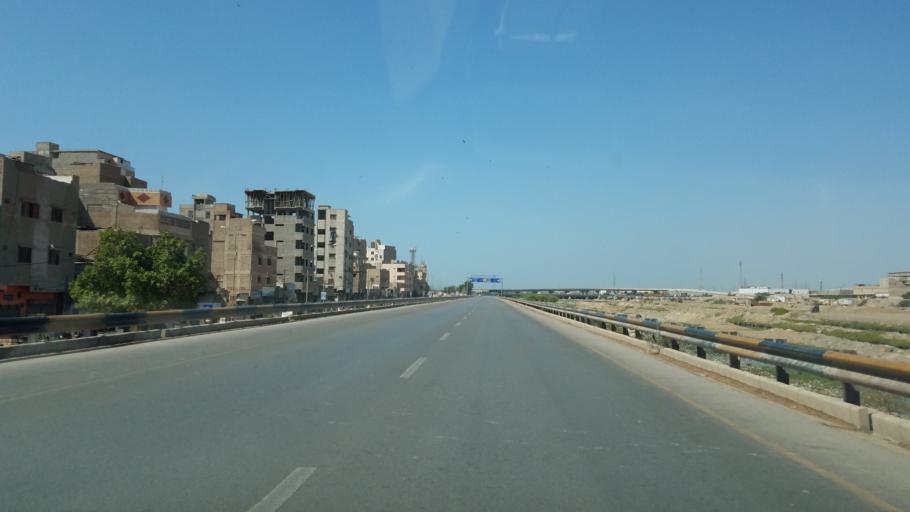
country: PK
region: Sindh
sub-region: Karachi District
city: Karachi
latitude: 24.8741
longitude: 66.9822
